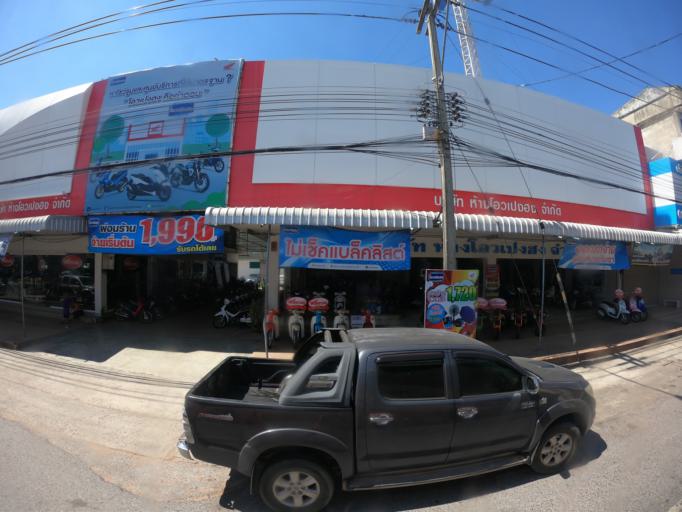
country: TH
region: Khon Kaen
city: Ban Phai
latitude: 16.0587
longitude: 102.7262
